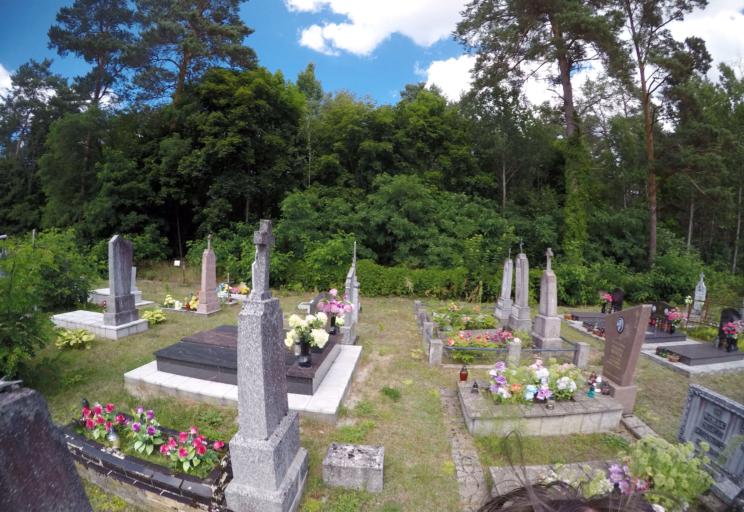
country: BY
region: Grodnenskaya
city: Skidal'
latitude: 53.8199
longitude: 24.2527
